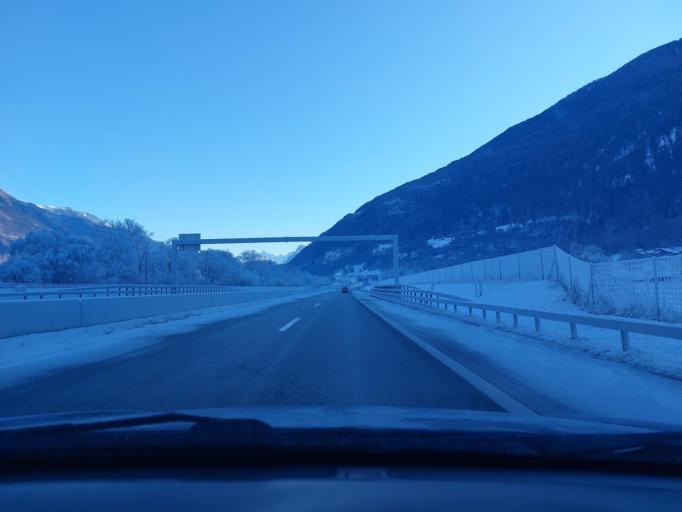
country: CH
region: Valais
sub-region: Leuk District
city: Gampel
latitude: 46.3071
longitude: 7.7280
